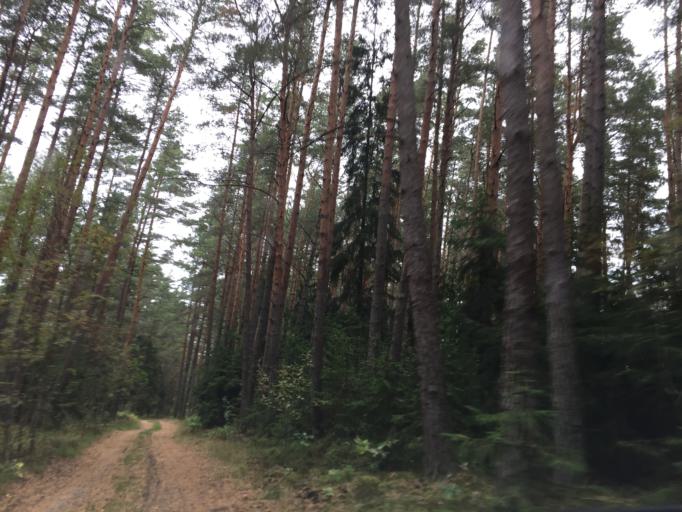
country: LV
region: Salacgrivas
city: Salacgriva
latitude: 57.7043
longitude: 24.3555
